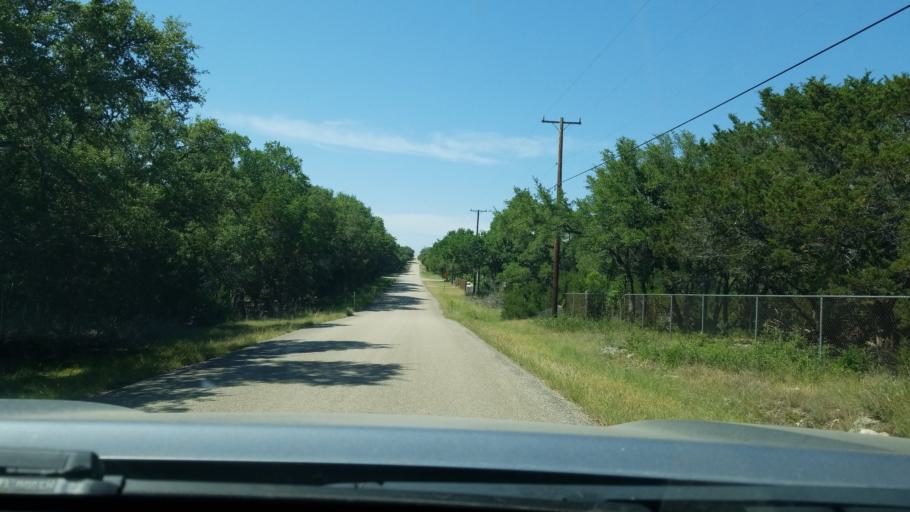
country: US
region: Texas
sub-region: Bexar County
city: Timberwood Park
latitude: 29.7570
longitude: -98.5153
